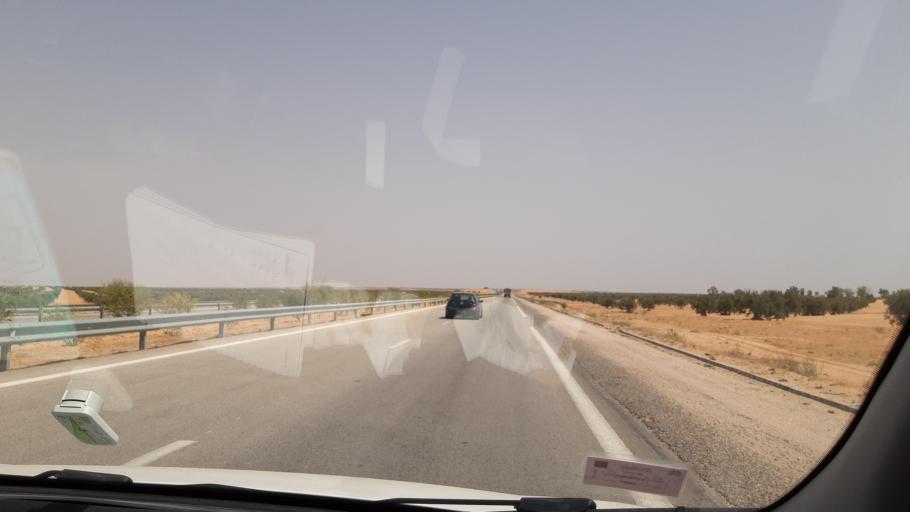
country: TN
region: Safaqis
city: Bi'r `Ali Bin Khalifah
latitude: 34.5302
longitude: 10.1072
